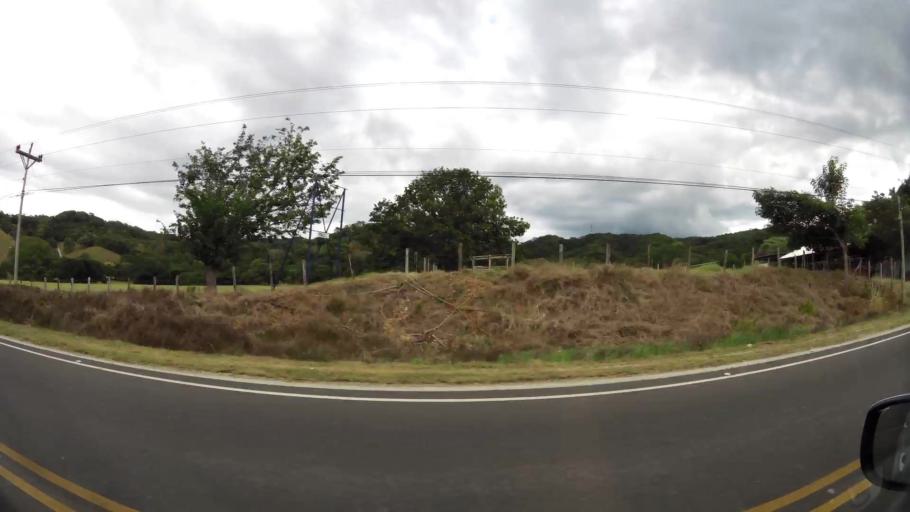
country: CR
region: Guanacaste
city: Nandayure
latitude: 10.2307
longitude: -85.2179
